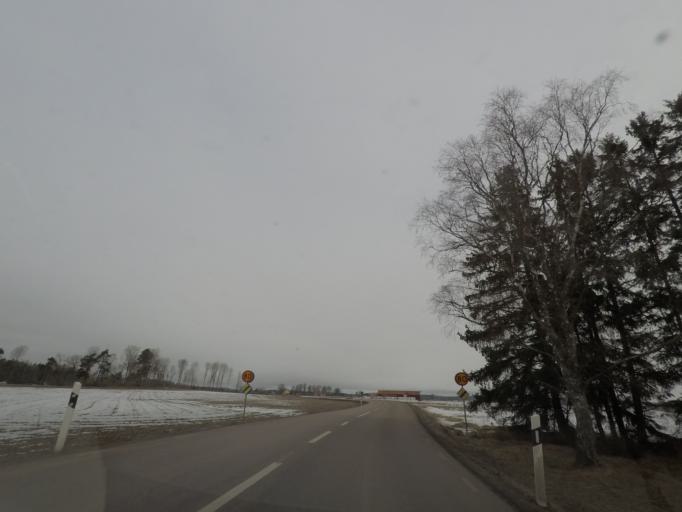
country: SE
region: Vaestmanland
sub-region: Vasteras
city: Skultuna
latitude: 59.7241
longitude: 16.4223
